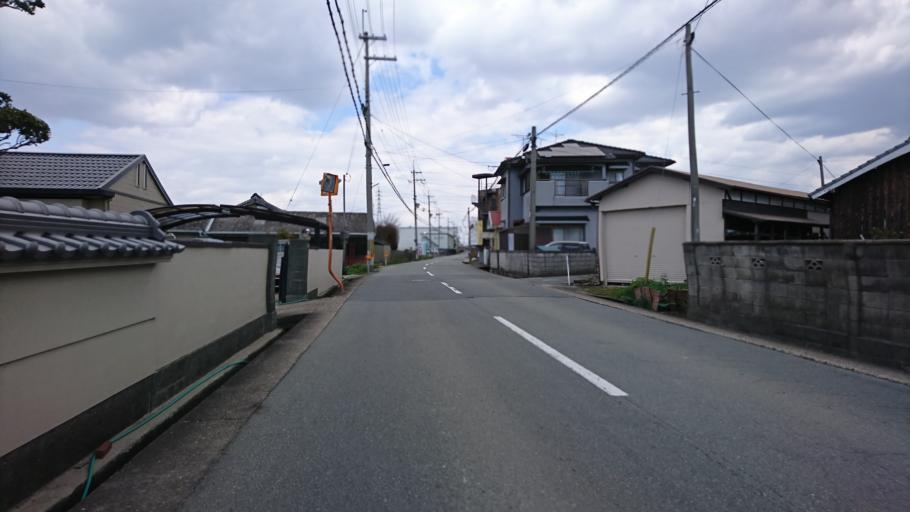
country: JP
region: Hyogo
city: Miki
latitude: 34.7392
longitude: 134.9290
